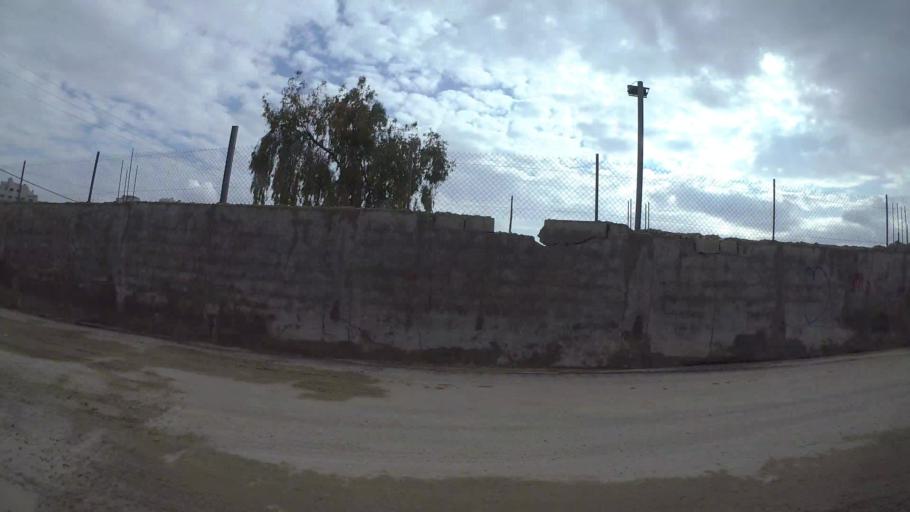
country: JO
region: Amman
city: Wadi as Sir
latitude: 31.9362
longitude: 35.8479
